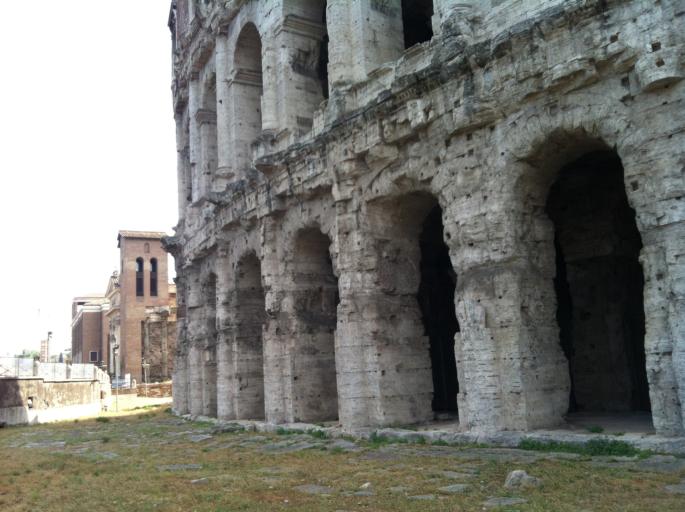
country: VA
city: Vatican City
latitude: 41.8922
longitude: 12.4799
